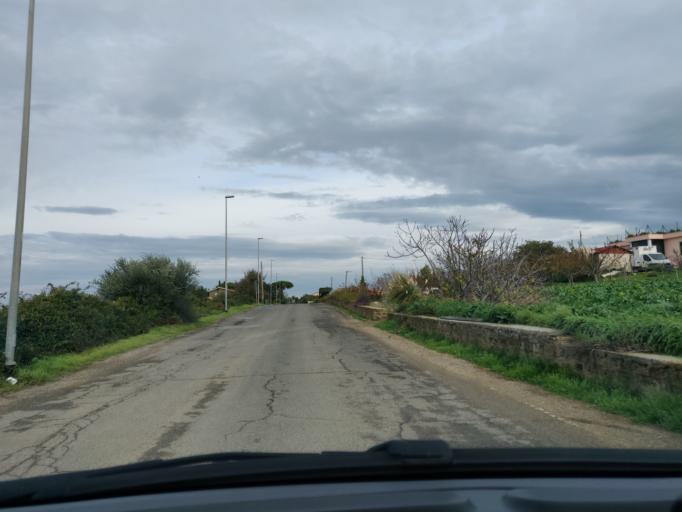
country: IT
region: Latium
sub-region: Citta metropolitana di Roma Capitale
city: Civitavecchia
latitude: 42.1013
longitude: 11.8130
